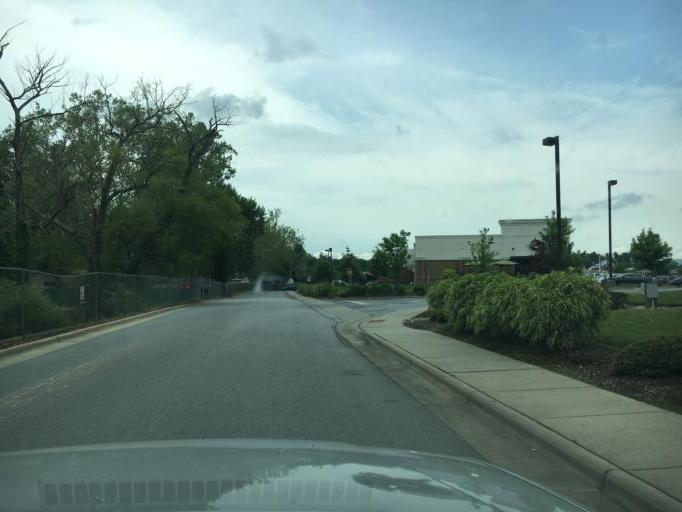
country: US
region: North Carolina
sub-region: Henderson County
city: Barker Heights
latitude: 35.3090
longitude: -82.4544
